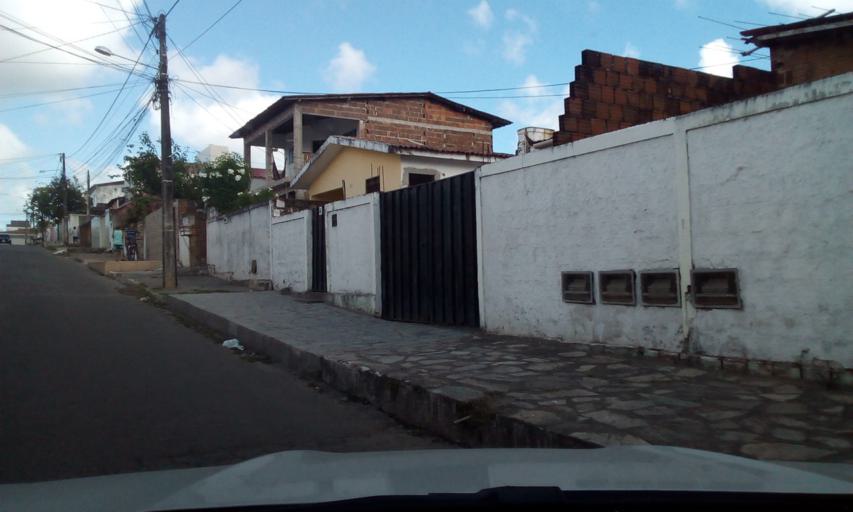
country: BR
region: Paraiba
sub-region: Joao Pessoa
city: Joao Pessoa
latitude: -7.1752
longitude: -34.8462
